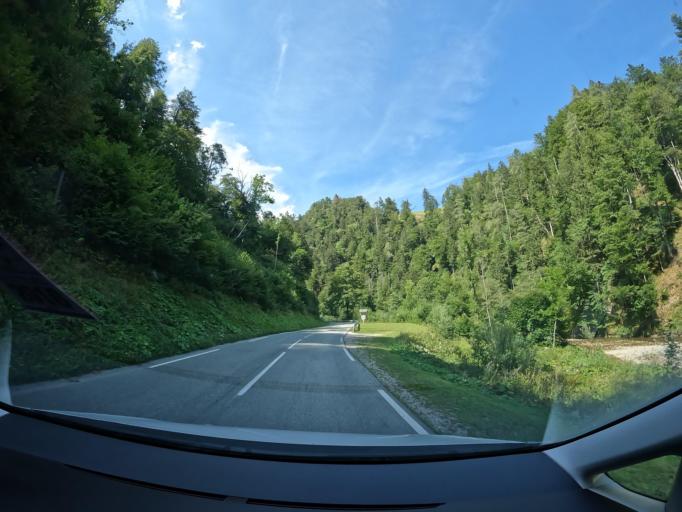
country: SI
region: Trzic
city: Trzic
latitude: 46.3884
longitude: 14.3605
